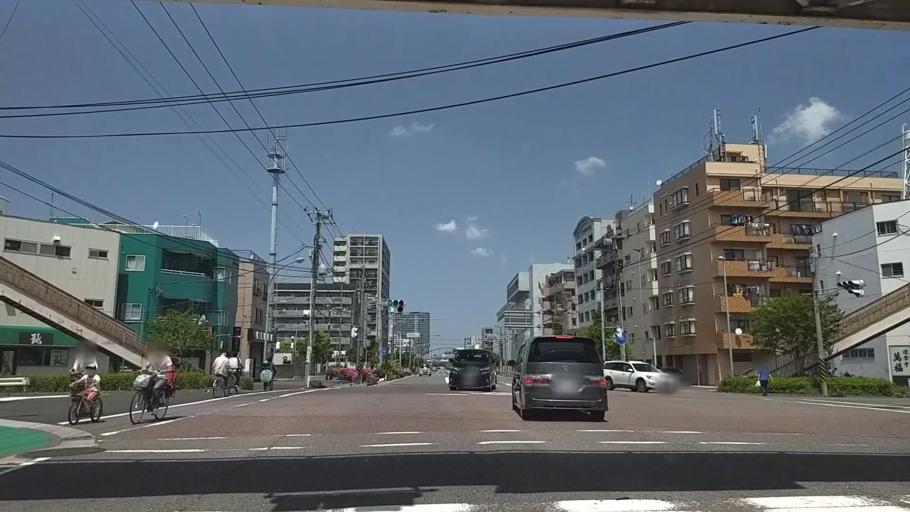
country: JP
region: Kanagawa
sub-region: Kawasaki-shi
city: Kawasaki
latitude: 35.5250
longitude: 139.7133
